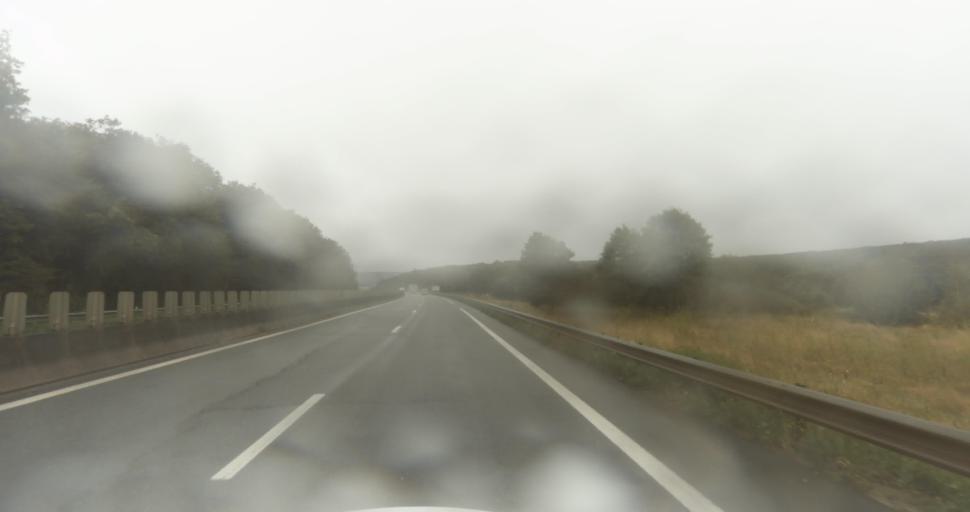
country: FR
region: Haute-Normandie
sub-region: Departement de l'Eure
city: Gravigny
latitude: 49.0491
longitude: 1.1806
